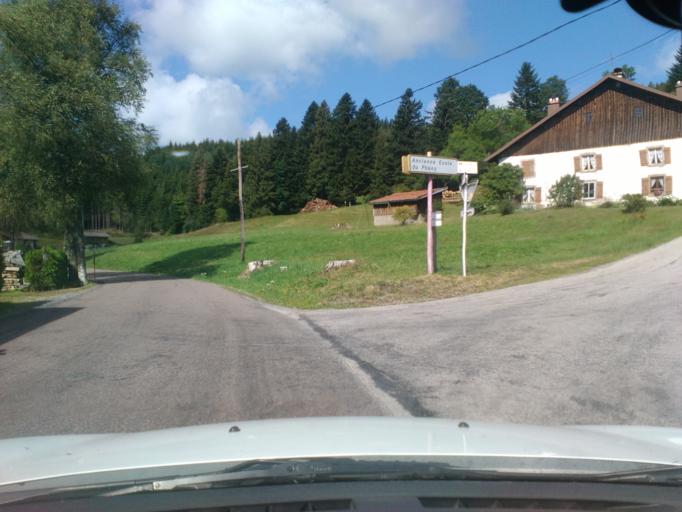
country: FR
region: Lorraine
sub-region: Departement des Vosges
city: Gerardmer
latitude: 48.0444
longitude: 6.8384
